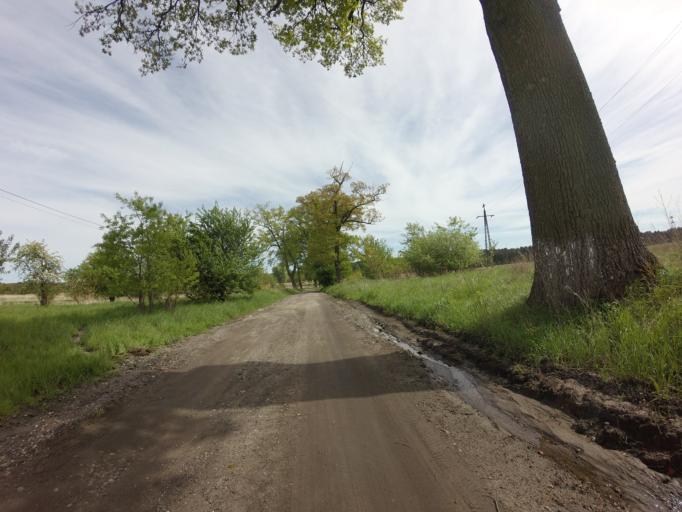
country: PL
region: West Pomeranian Voivodeship
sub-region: Powiat choszczenski
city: Recz
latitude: 53.1584
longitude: 15.6088
